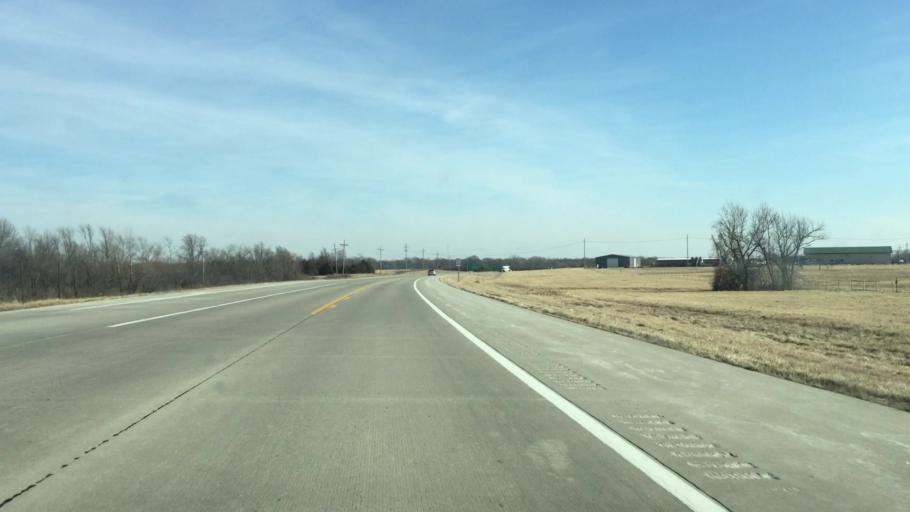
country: US
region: Kansas
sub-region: Labette County
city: Parsons
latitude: 37.3681
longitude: -95.2934
